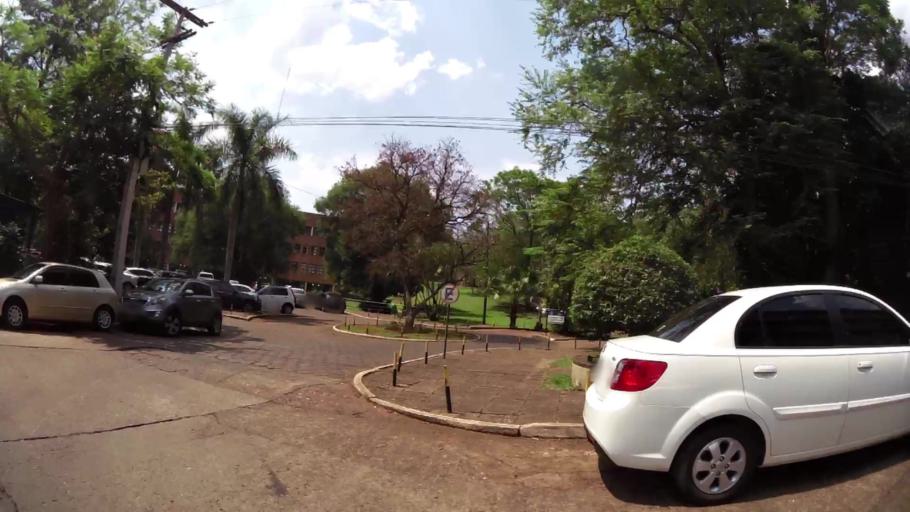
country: PY
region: Alto Parana
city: Ciudad del Este
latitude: -25.4767
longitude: -54.6233
